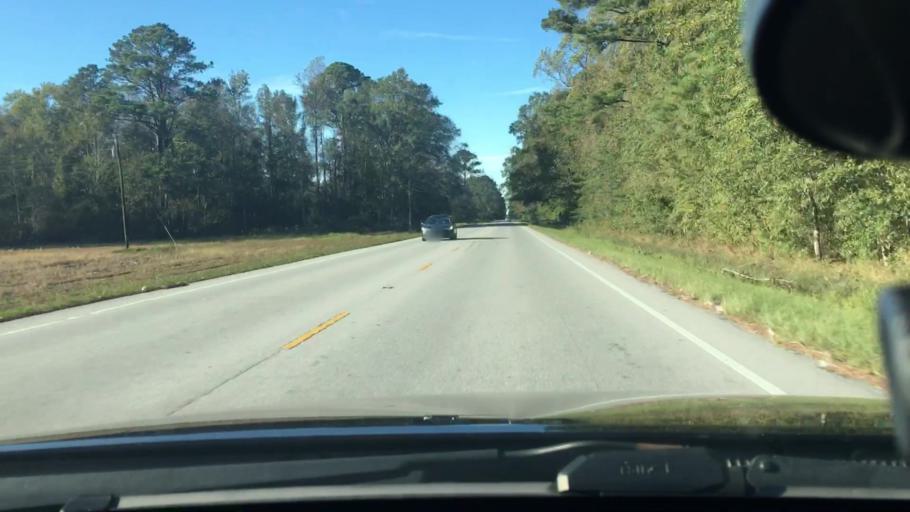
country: US
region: North Carolina
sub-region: Craven County
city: New Bern
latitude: 35.1775
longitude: -77.0461
